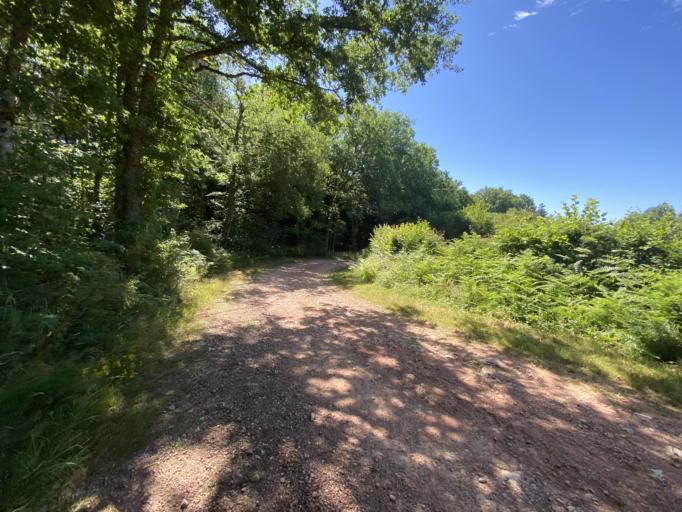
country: FR
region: Bourgogne
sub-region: Departement de la Cote-d'Or
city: Saulieu
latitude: 47.2908
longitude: 4.1285
